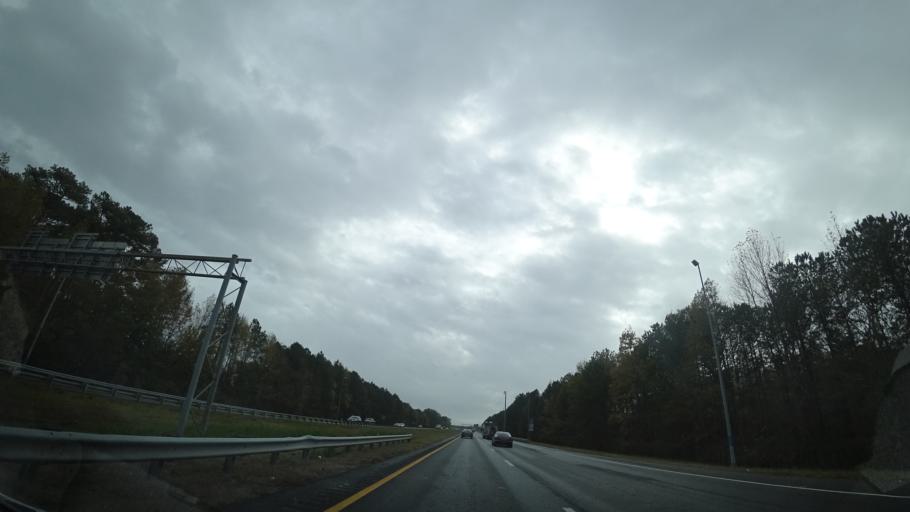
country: US
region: Virginia
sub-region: City of Portsmouth
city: Portsmouth Heights
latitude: 36.8131
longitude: -76.4316
